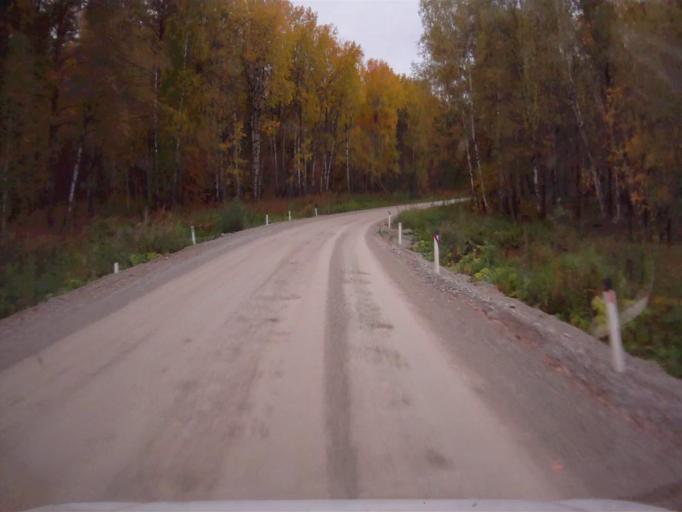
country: RU
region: Chelyabinsk
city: Nyazepetrovsk
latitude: 56.0683
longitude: 59.4337
